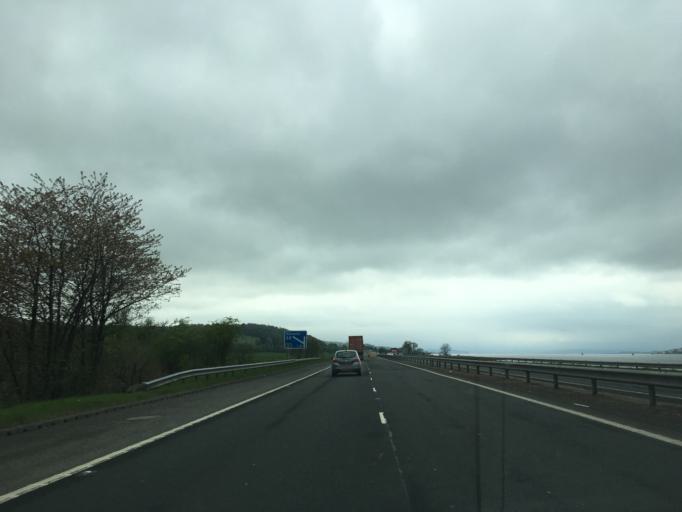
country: GB
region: Scotland
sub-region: Renfrewshire
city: Bishopton
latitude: 55.9227
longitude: -4.5342
